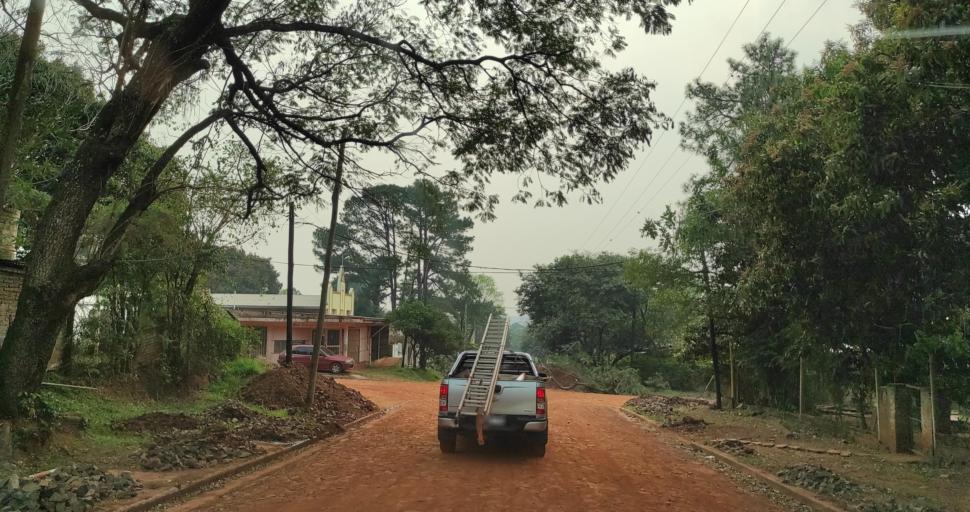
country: AR
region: Misiones
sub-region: Departamento de Capital
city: Posadas
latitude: -27.4275
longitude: -55.8911
